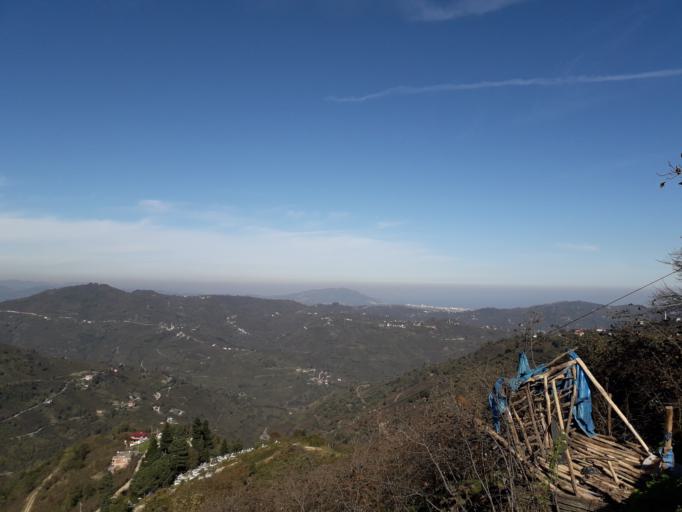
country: TR
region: Ordu
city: Ordu
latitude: 40.9531
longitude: 37.8956
